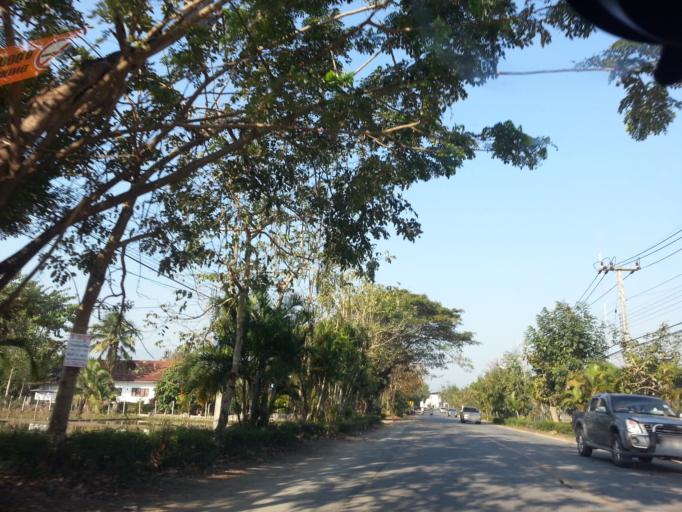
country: TH
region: Chiang Mai
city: San Sai
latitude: 18.8757
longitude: 99.0468
